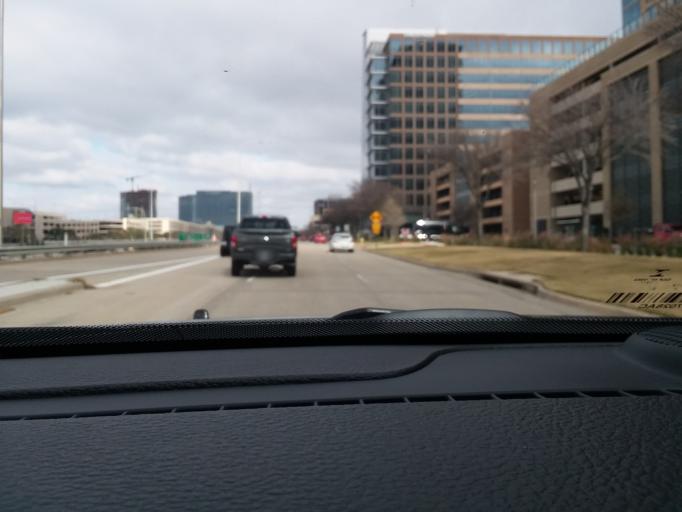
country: US
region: Texas
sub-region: Denton County
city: The Colony
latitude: 33.0759
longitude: -96.8240
